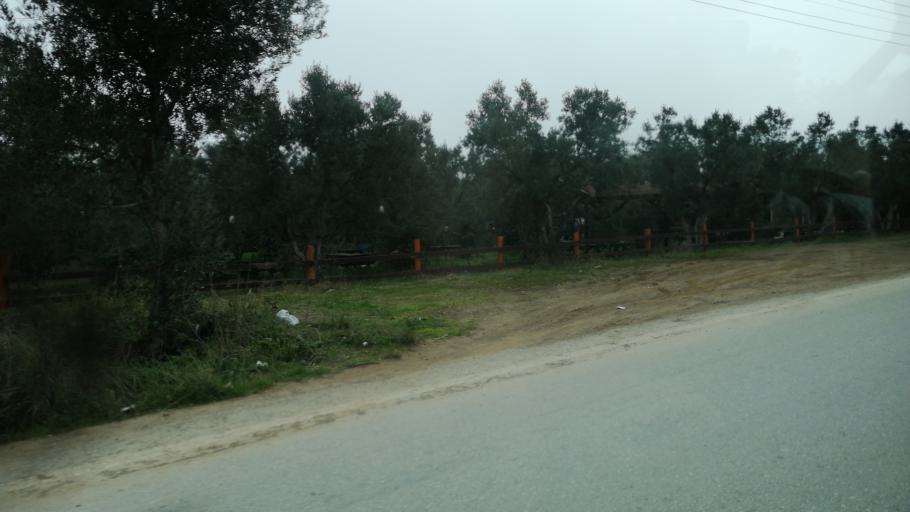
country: TR
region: Yalova
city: Cinarcik
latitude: 40.6391
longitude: 29.0818
